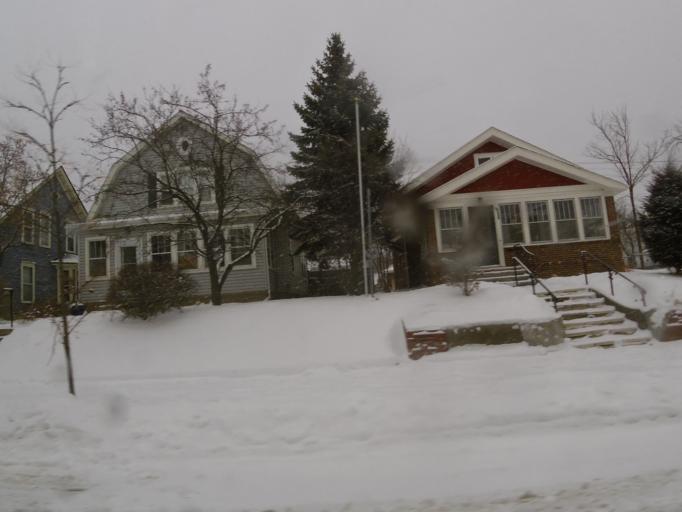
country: US
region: Minnesota
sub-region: Hennepin County
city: Minneapolis
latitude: 44.9326
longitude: -93.2612
